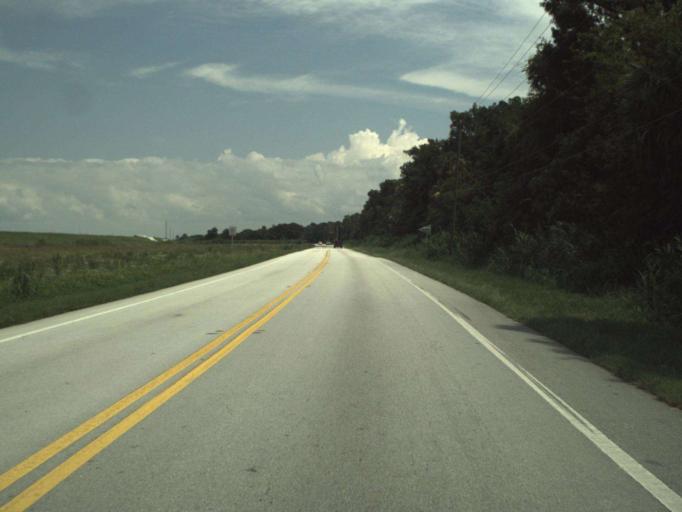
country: US
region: Florida
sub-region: Martin County
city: Indiantown
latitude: 26.9593
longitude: -80.6096
